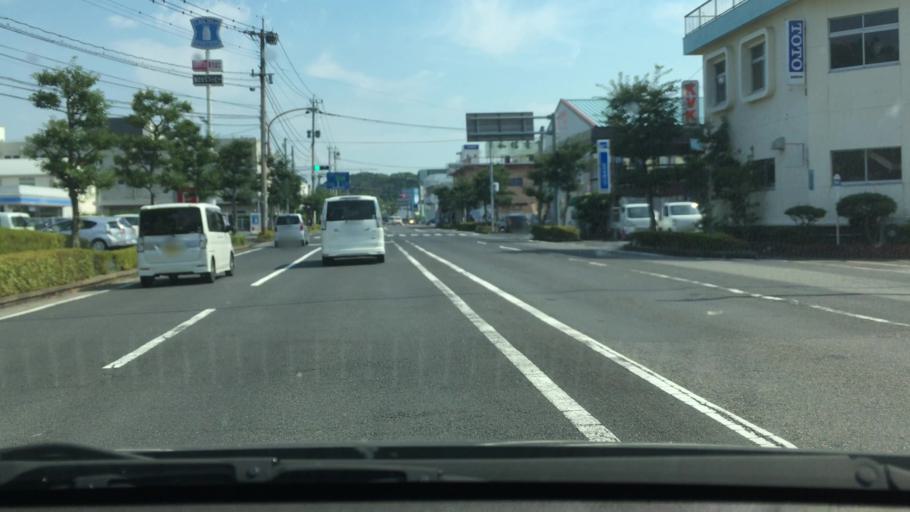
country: JP
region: Nagasaki
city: Sasebo
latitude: 33.1518
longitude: 129.7707
